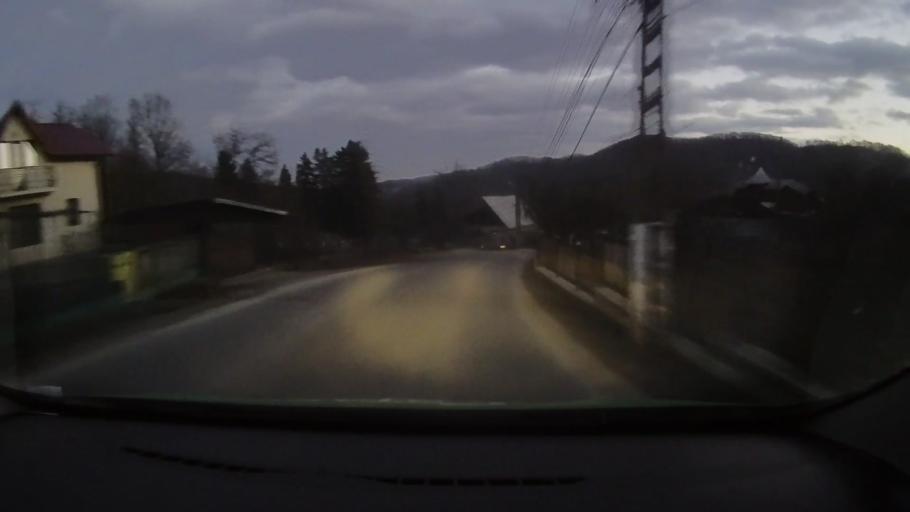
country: RO
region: Prahova
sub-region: Comuna Provita de Jos
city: Provita de Jos
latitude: 45.1231
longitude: 25.6610
